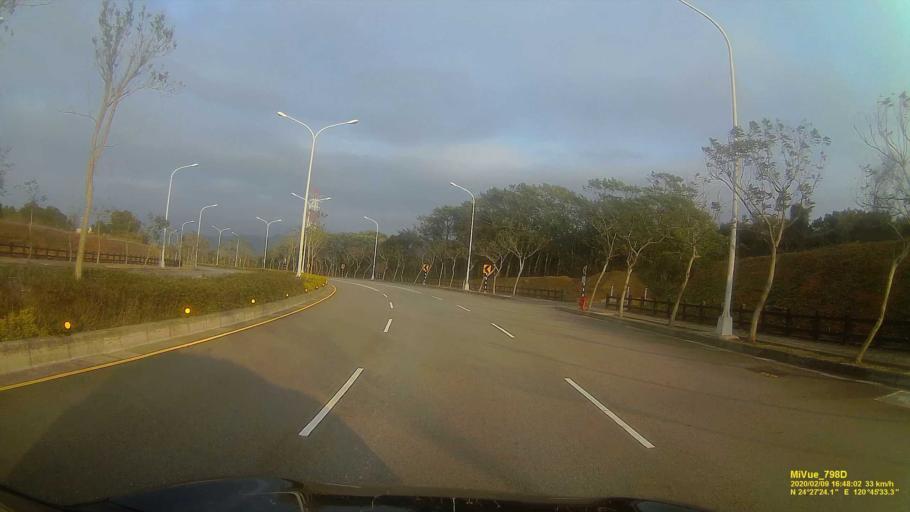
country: TW
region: Taiwan
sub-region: Miaoli
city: Miaoli
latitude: 24.4565
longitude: 120.7595
